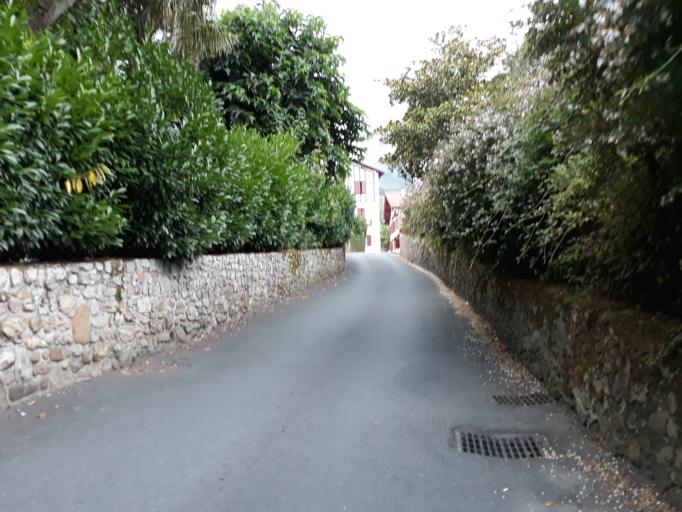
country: FR
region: Aquitaine
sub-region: Departement des Pyrenees-Atlantiques
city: Ascain
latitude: 43.3460
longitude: -1.6219
